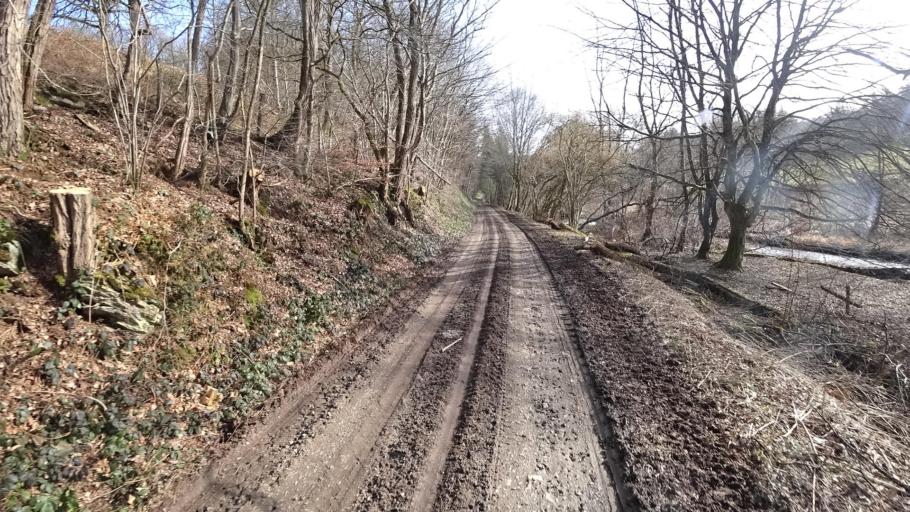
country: DE
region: Rheinland-Pfalz
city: Scheuerfeld
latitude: 50.7691
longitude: 7.8343
